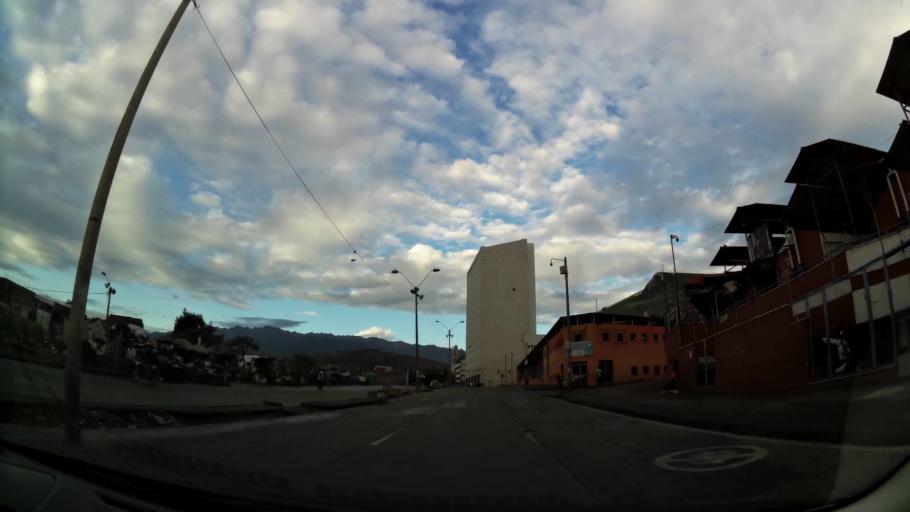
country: CO
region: Valle del Cauca
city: Cali
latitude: 3.4479
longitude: -76.5288
